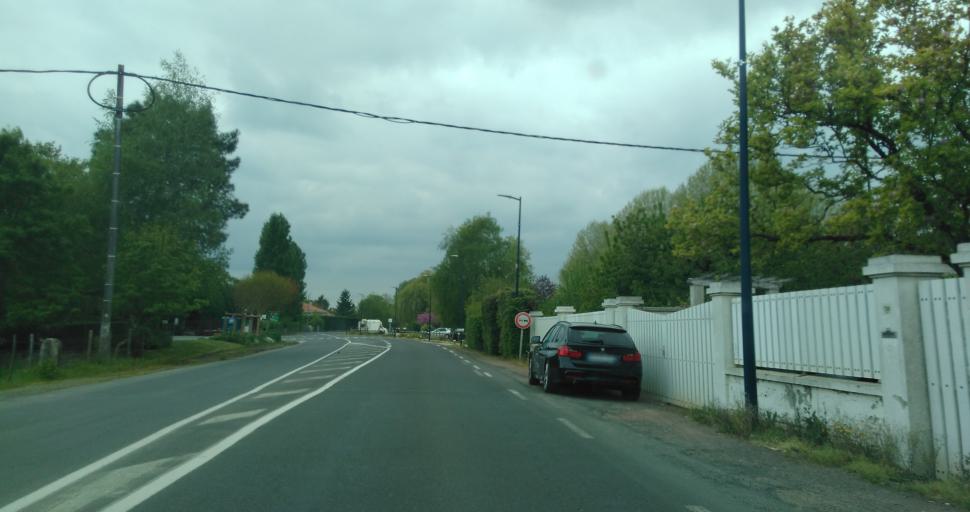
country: FR
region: Poitou-Charentes
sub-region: Departement des Deux-Sevres
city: Magne
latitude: 46.3131
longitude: -0.5336
